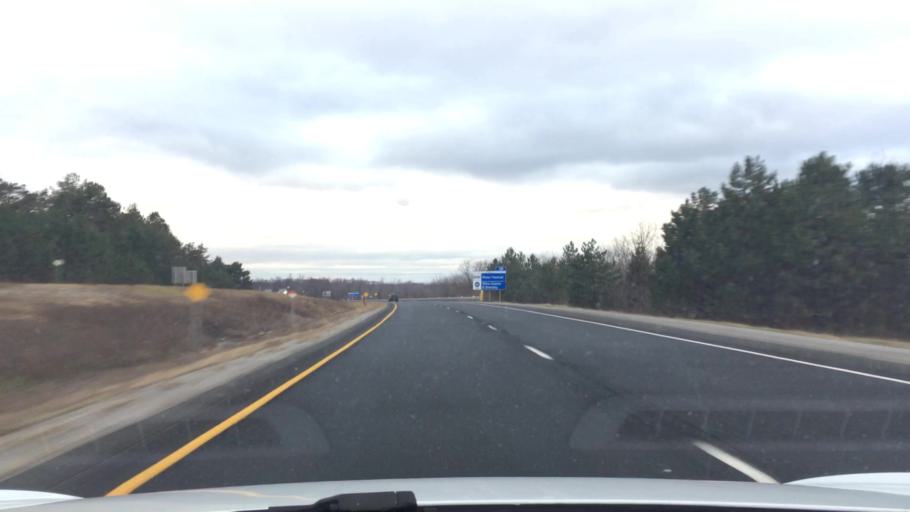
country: CA
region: Ontario
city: Niagara Falls
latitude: 43.1527
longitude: -79.1239
